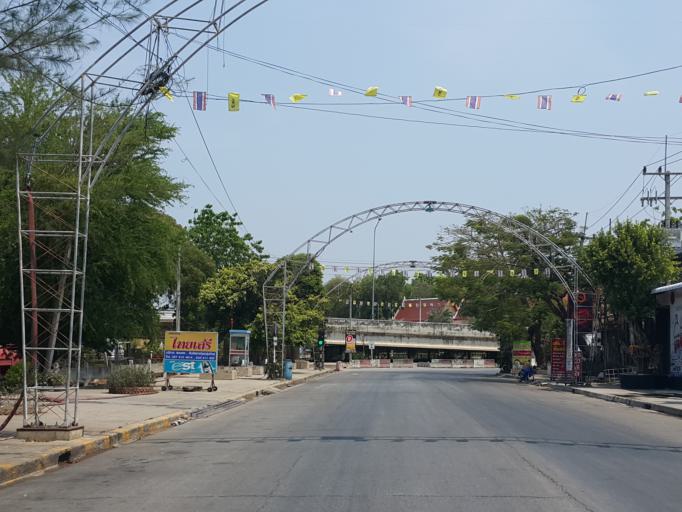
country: TH
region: Kanchanaburi
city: Kanchanaburi
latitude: 14.0246
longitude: 99.5264
